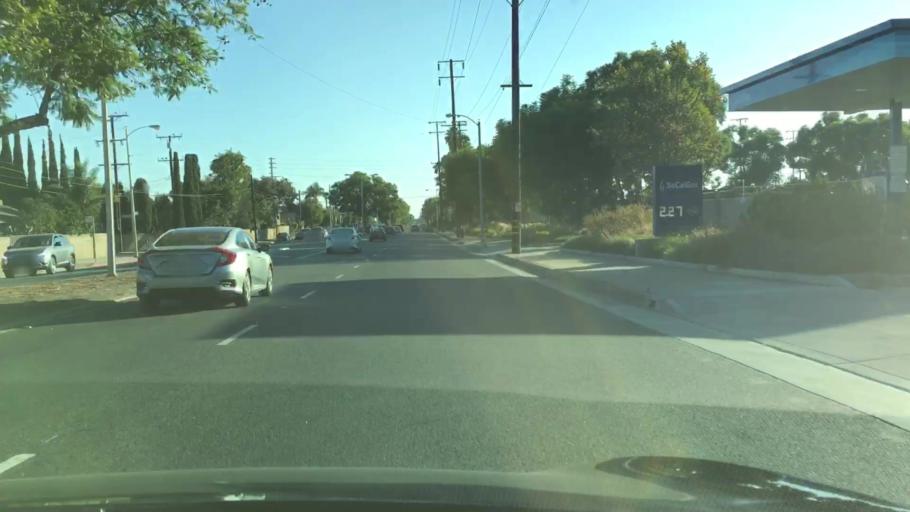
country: US
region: California
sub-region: Los Angeles County
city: Pico Rivera
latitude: 33.9686
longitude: -118.1062
